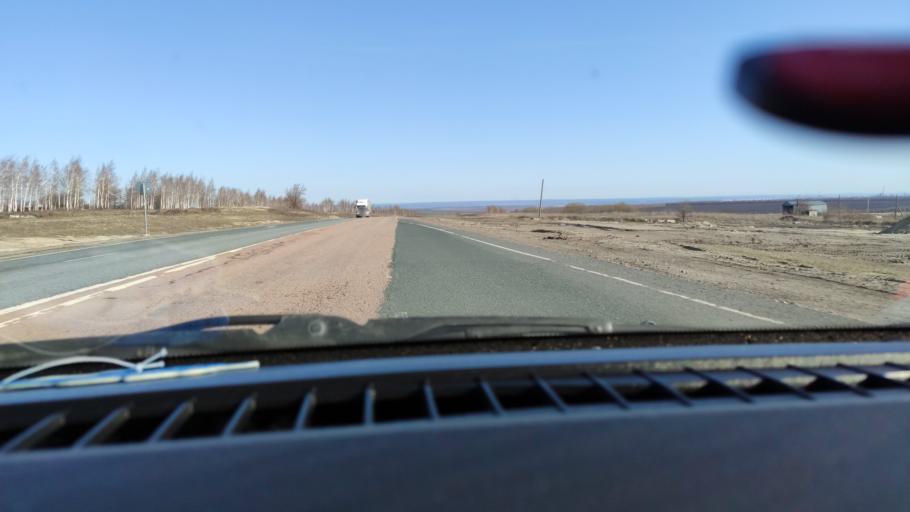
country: RU
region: Samara
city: Syzran'
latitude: 52.9580
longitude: 48.3074
